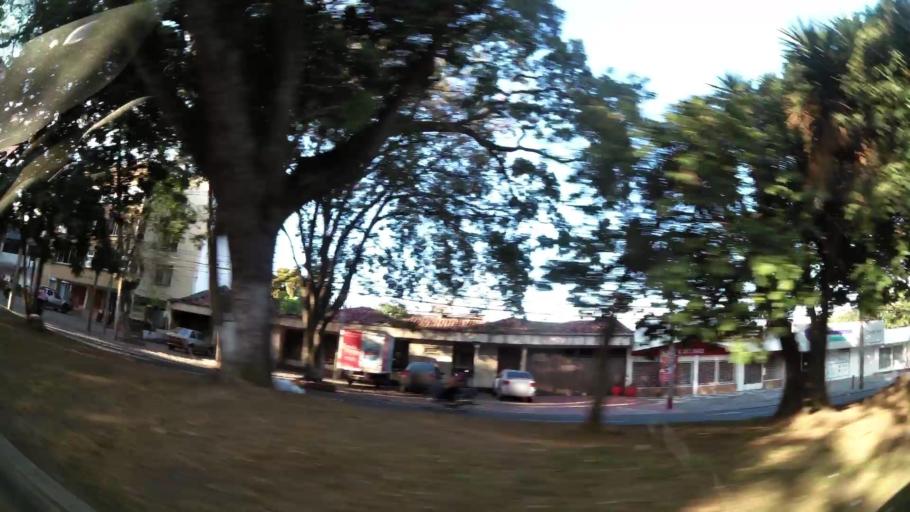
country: CO
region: Valle del Cauca
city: Cali
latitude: 3.4810
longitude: -76.5231
